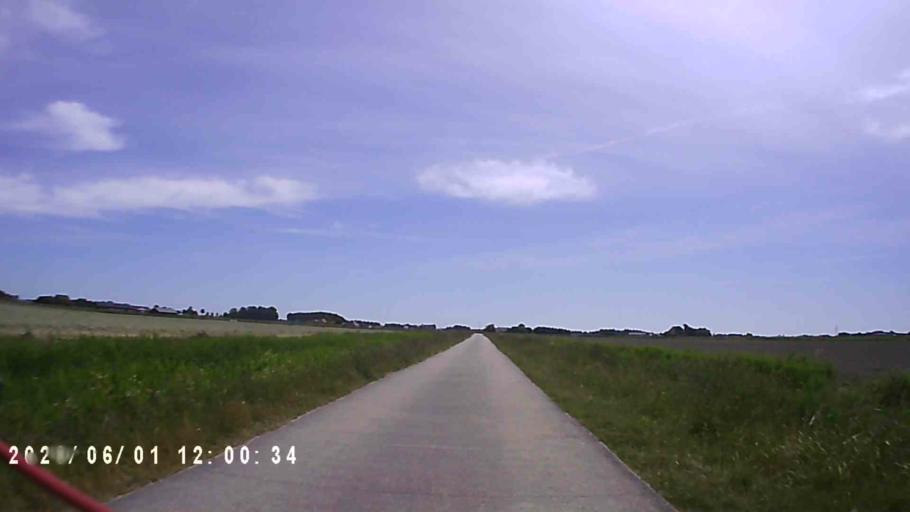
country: NL
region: Friesland
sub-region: Gemeente Harlingen
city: Harlingen
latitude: 53.1586
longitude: 5.4504
